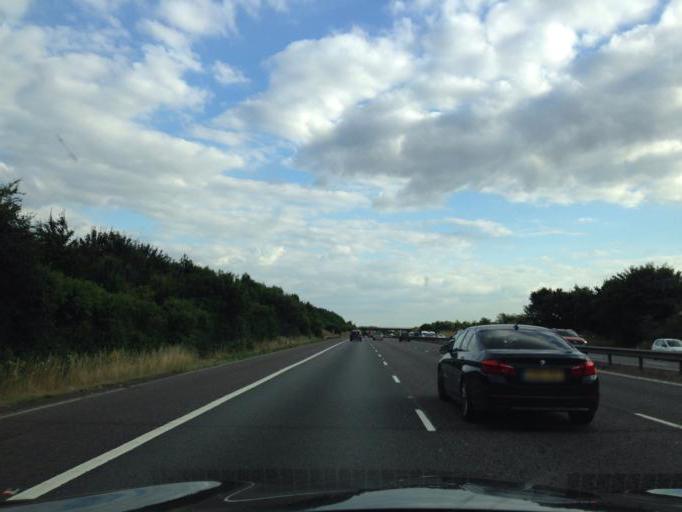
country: GB
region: England
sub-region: Oxfordshire
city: Bicester
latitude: 51.8987
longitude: -1.2060
